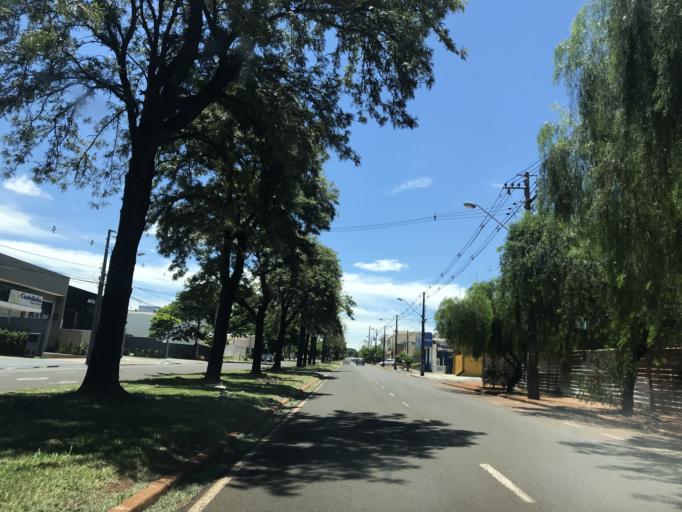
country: BR
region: Parana
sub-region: Maringa
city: Maringa
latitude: -23.4493
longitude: -51.9288
